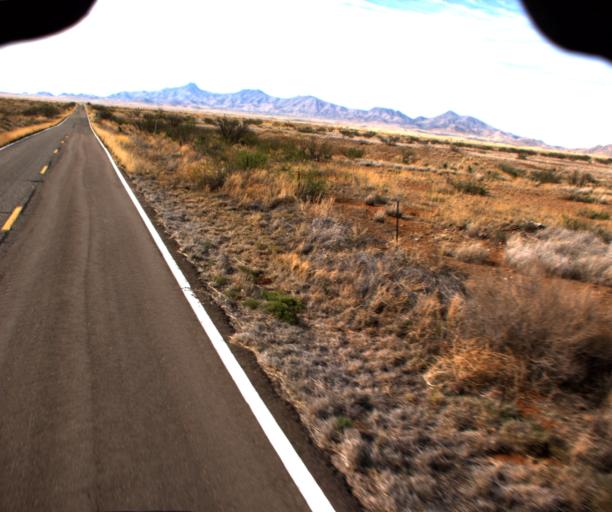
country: US
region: Arizona
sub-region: Cochise County
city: Willcox
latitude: 32.0460
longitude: -109.4869
